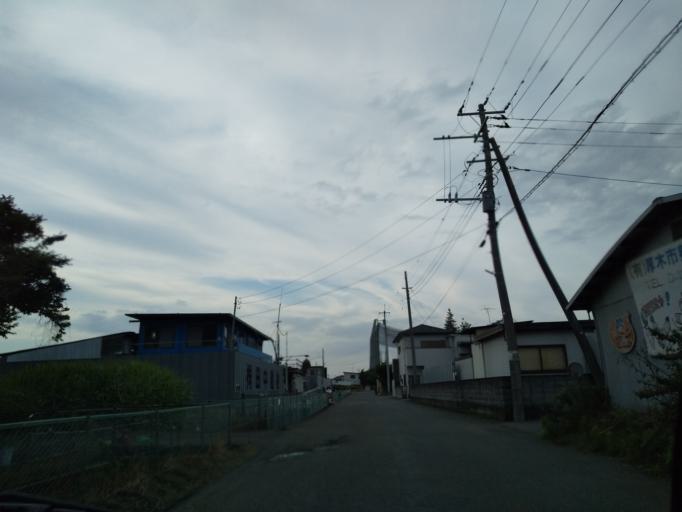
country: JP
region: Kanagawa
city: Atsugi
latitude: 35.4708
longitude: 139.3616
